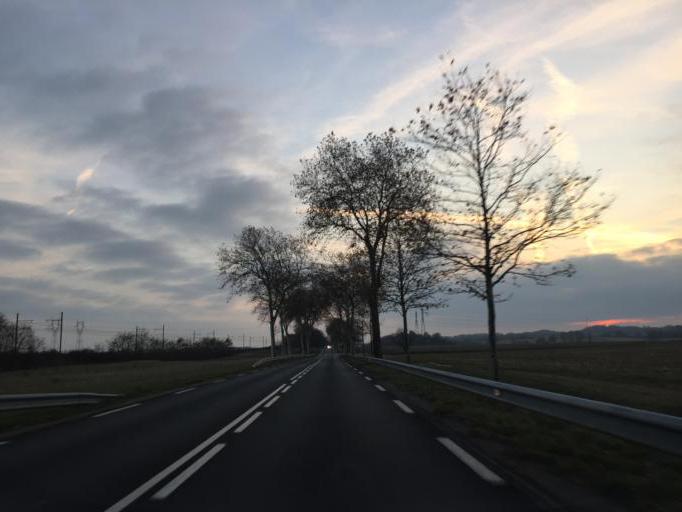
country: FR
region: Rhone-Alpes
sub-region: Departement de l'Ain
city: Beligneux
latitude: 45.8756
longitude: 5.1595
